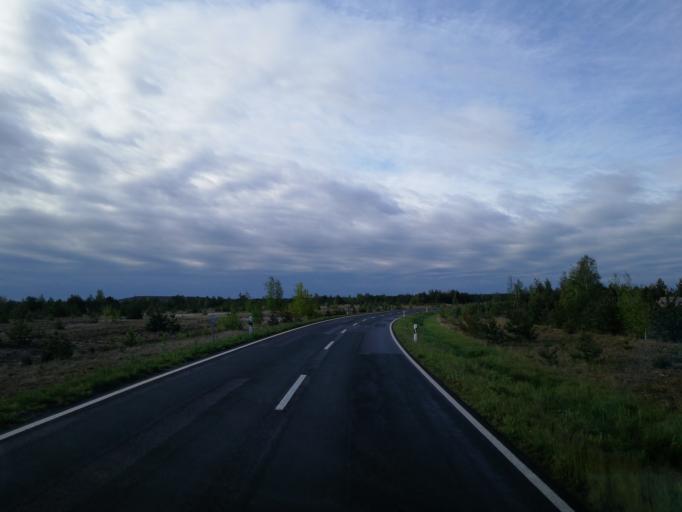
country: DE
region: Brandenburg
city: Sallgast
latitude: 51.5677
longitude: 13.7790
